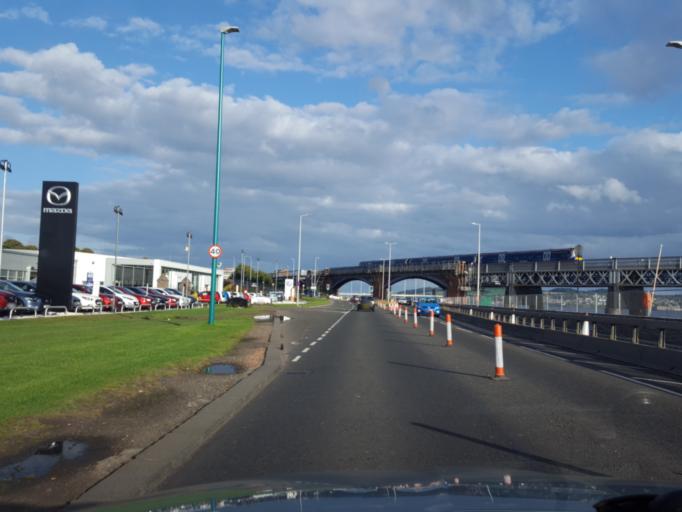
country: GB
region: Scotland
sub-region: Dundee City
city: Dundee
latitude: 56.4515
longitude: -2.9931
